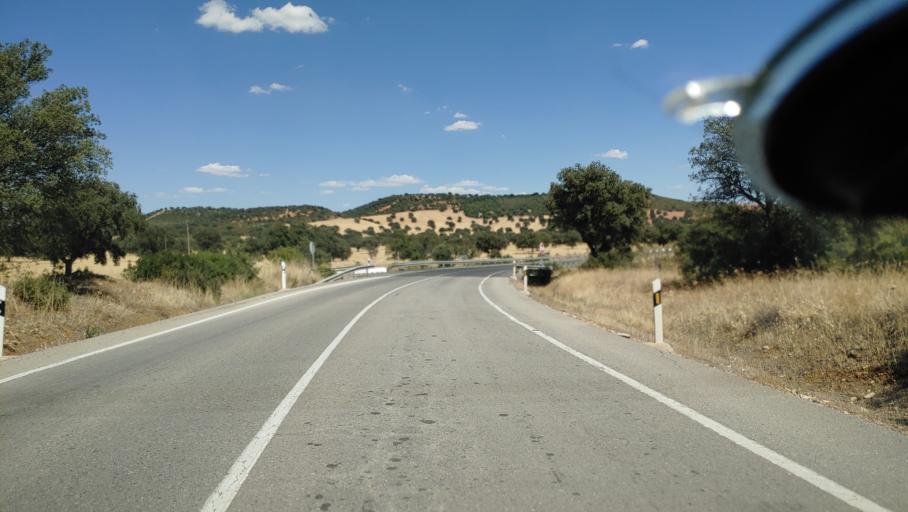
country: ES
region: Castille-La Mancha
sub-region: Provincia de Ciudad Real
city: Saceruela
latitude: 39.0167
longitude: -4.4803
